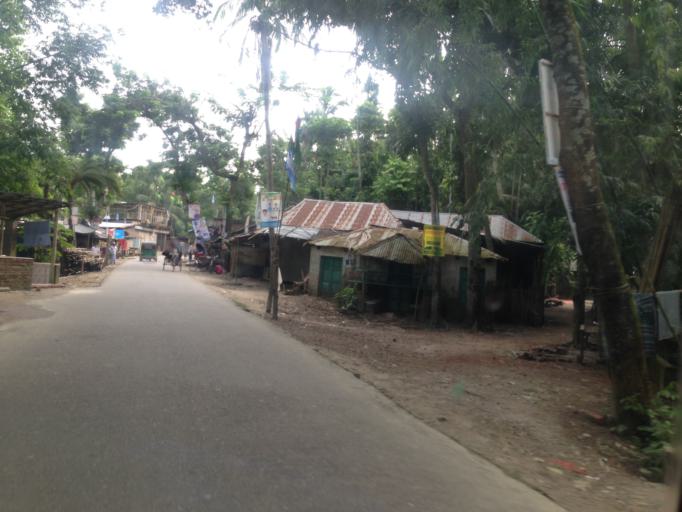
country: BD
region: Chittagong
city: Raipur
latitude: 23.0304
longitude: 90.7084
